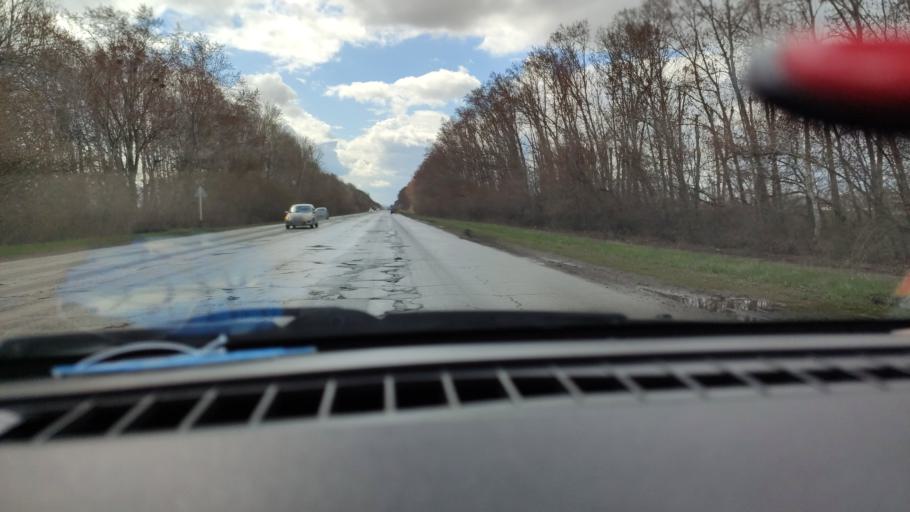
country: RU
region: Samara
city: Tol'yatti
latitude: 53.6257
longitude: 49.4160
